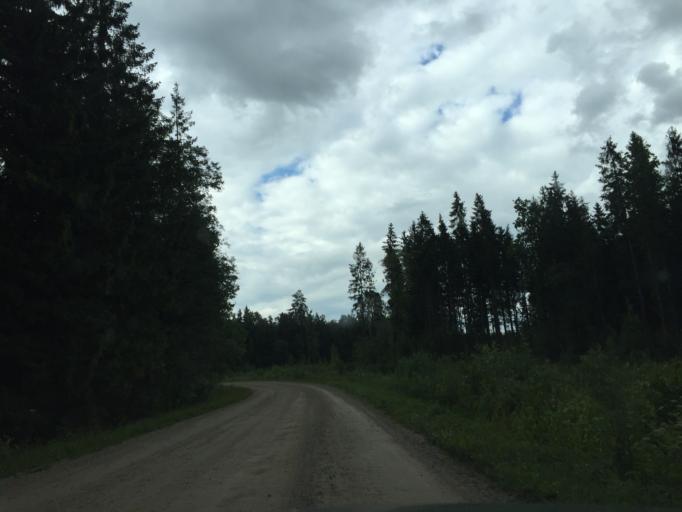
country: LV
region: Malpils
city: Malpils
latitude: 56.9437
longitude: 25.0033
